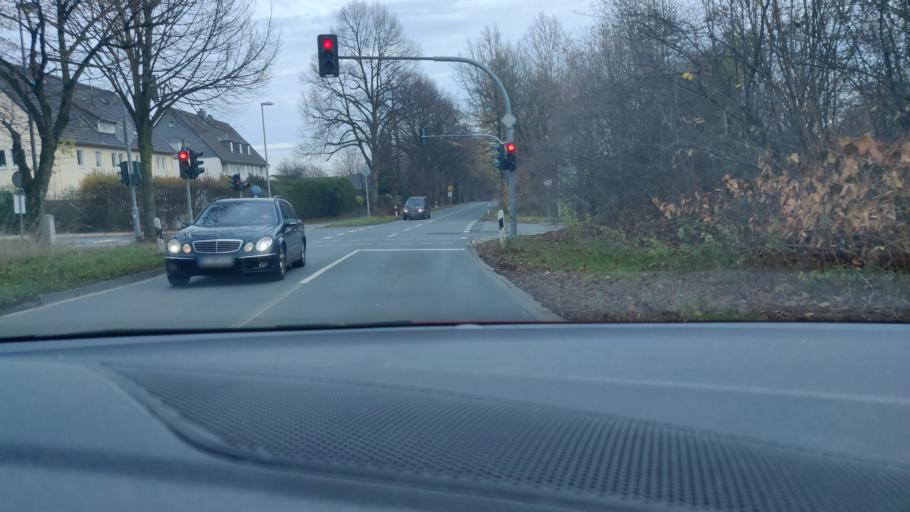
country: DE
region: North Rhine-Westphalia
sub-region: Regierungsbezirk Dusseldorf
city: Heiligenhaus
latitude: 51.3315
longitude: 6.9871
